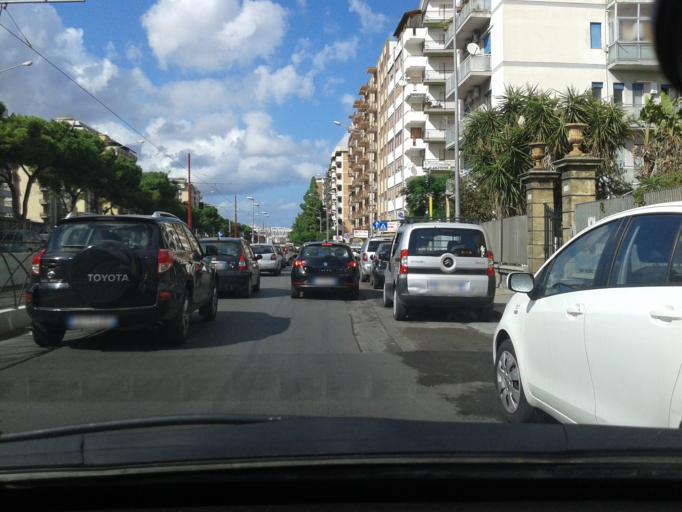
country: IT
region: Sicily
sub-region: Palermo
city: Palermo
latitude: 38.1223
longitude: 13.3293
